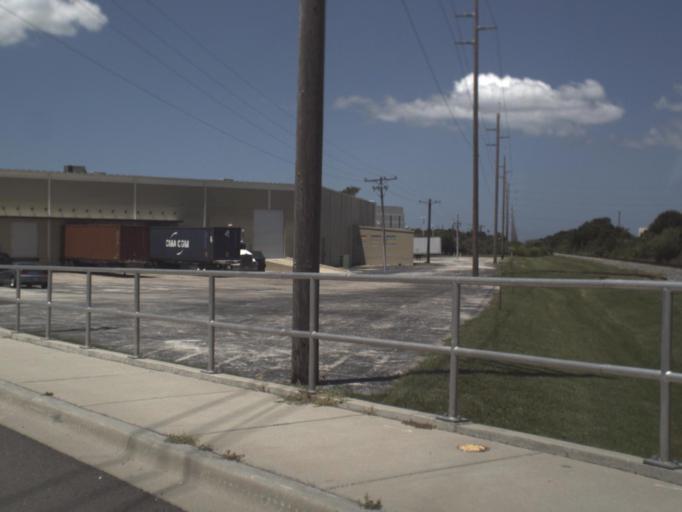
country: US
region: Florida
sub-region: Pinellas County
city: Seminole
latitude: 27.8724
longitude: -82.7503
